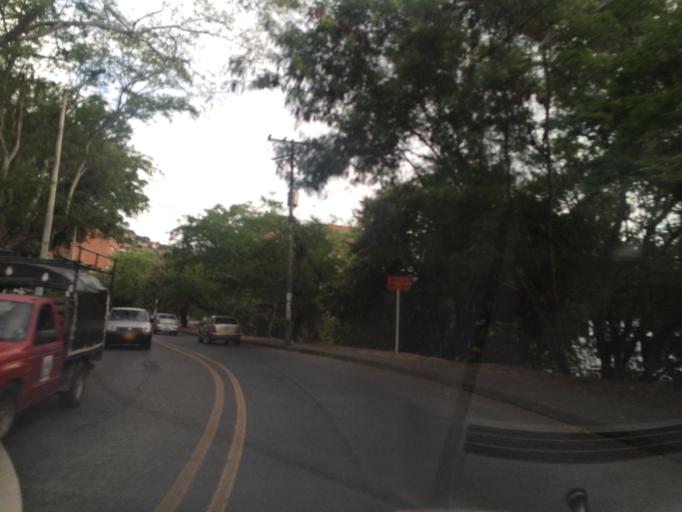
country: CO
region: Valle del Cauca
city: Cali
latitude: 3.4390
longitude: -76.5460
